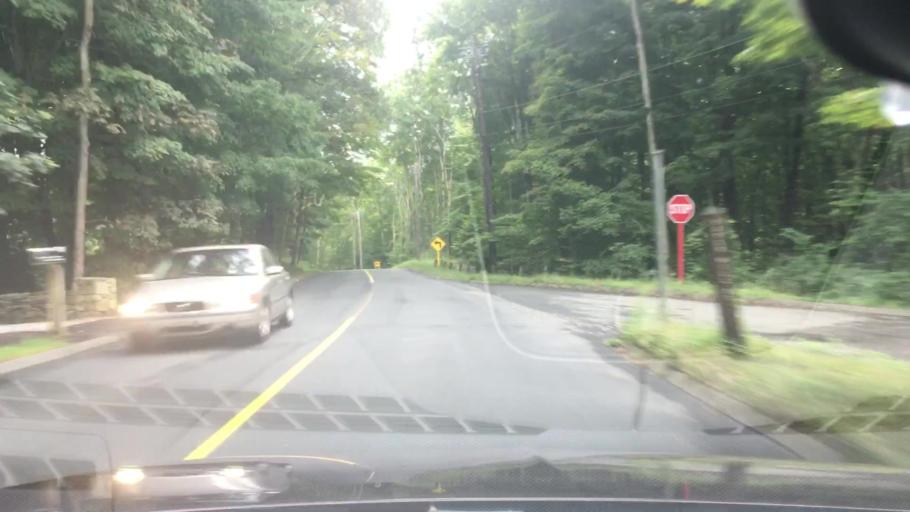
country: US
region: Connecticut
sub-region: New Haven County
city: Madison
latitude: 41.3259
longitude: -72.5925
